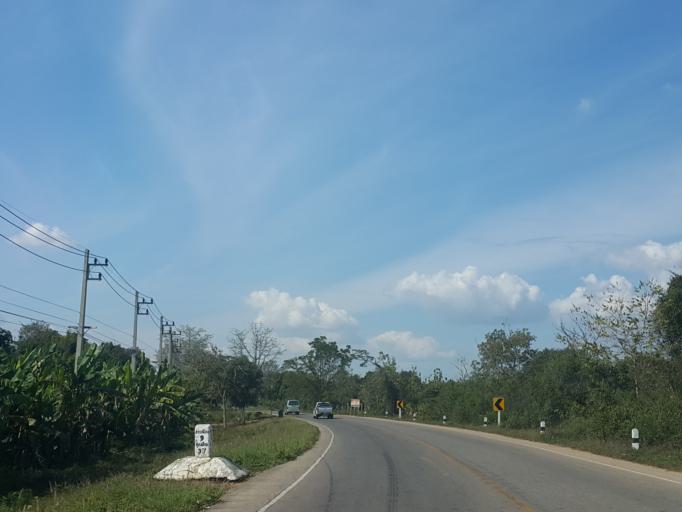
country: TH
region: Sukhothai
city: Sawankhalok
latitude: 17.2496
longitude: 99.8462
